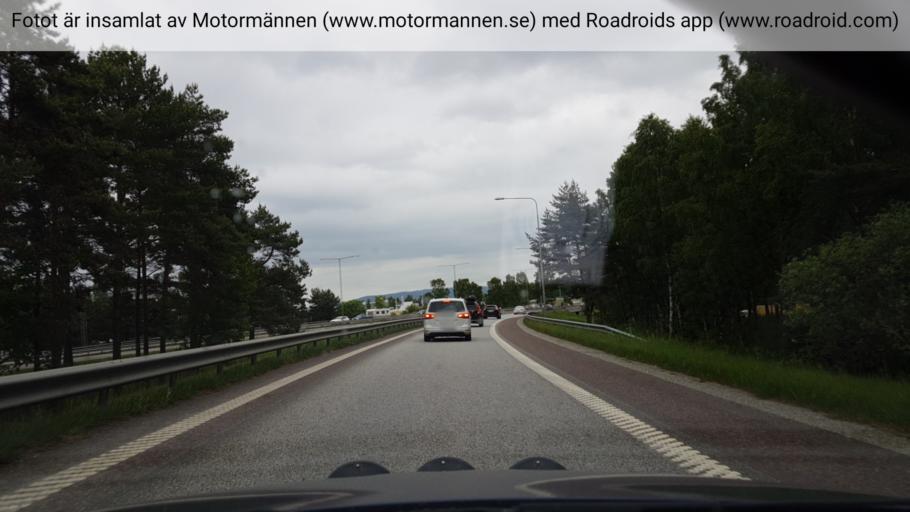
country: SE
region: Joenkoeping
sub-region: Jonkopings Kommun
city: Jonkoping
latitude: 57.7577
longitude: 14.1596
